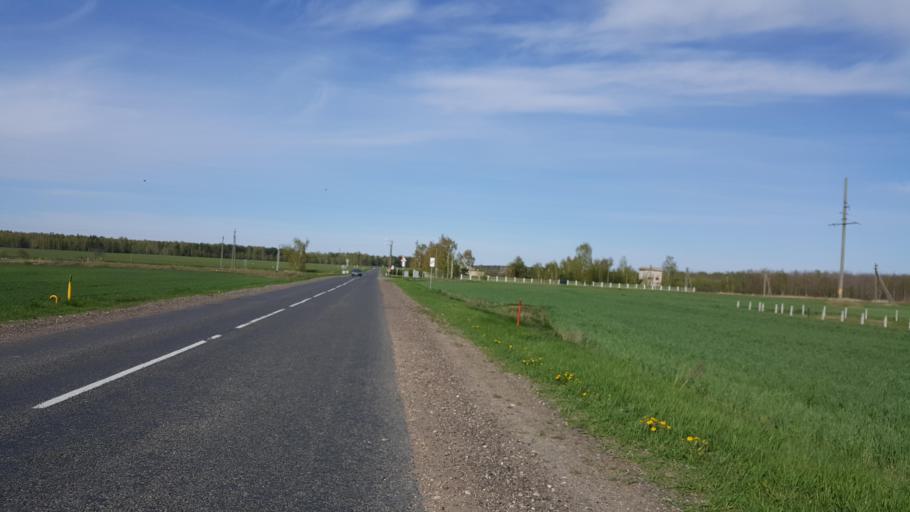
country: BY
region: Brest
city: Vysokaye
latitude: 52.3930
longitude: 23.4667
